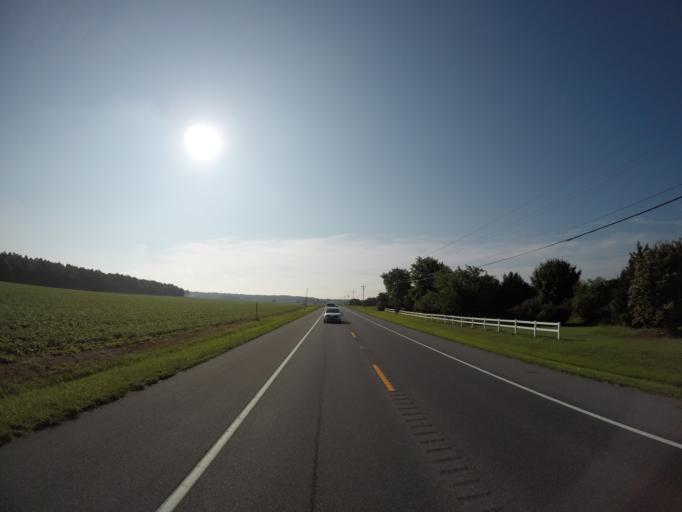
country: US
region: Delaware
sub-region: Sussex County
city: Georgetown
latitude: 38.6984
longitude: -75.4959
